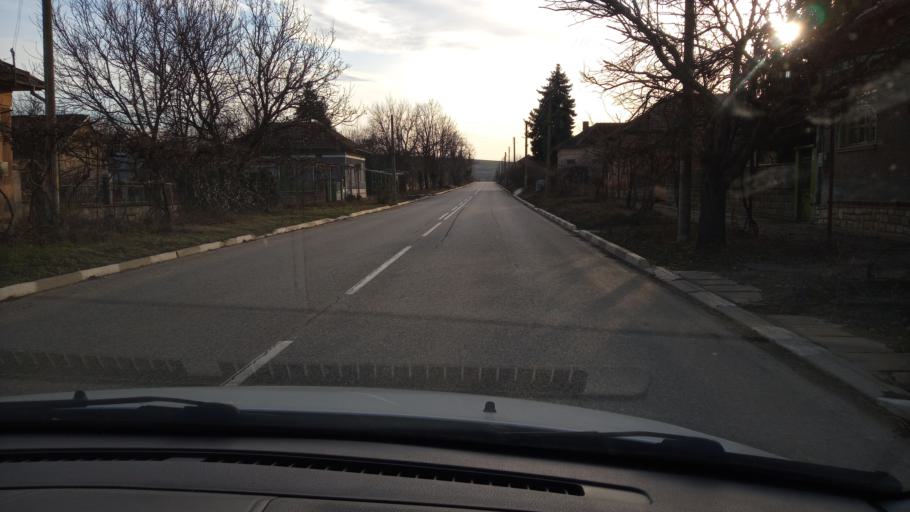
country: BG
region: Pleven
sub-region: Obshtina Pleven
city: Slavyanovo
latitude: 43.5525
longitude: 24.8644
